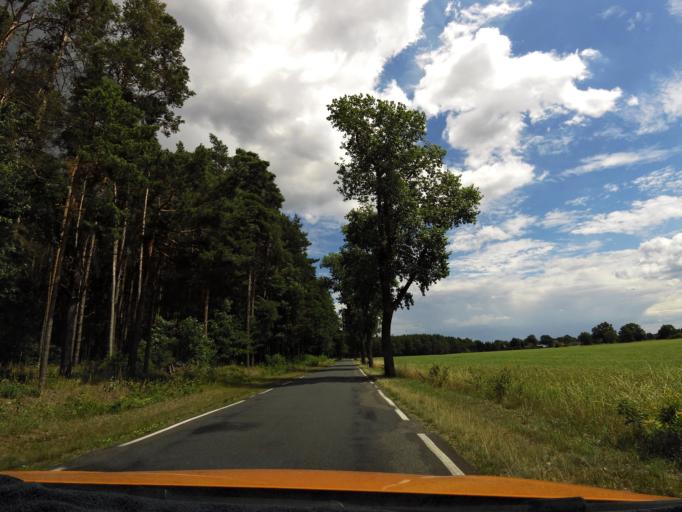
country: DE
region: Brandenburg
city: Storkow
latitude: 52.2460
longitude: 13.8575
